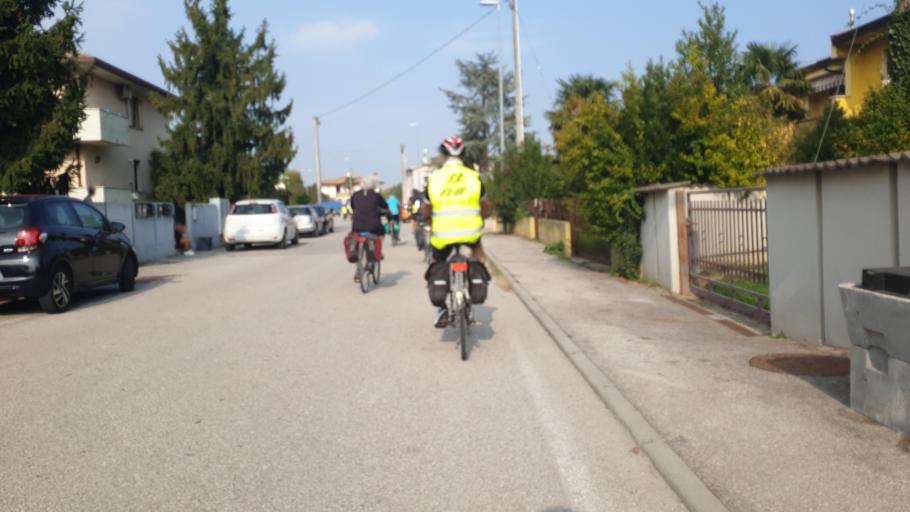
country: IT
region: Veneto
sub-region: Provincia di Padova
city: Vallonga
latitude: 45.2852
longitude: 12.0829
